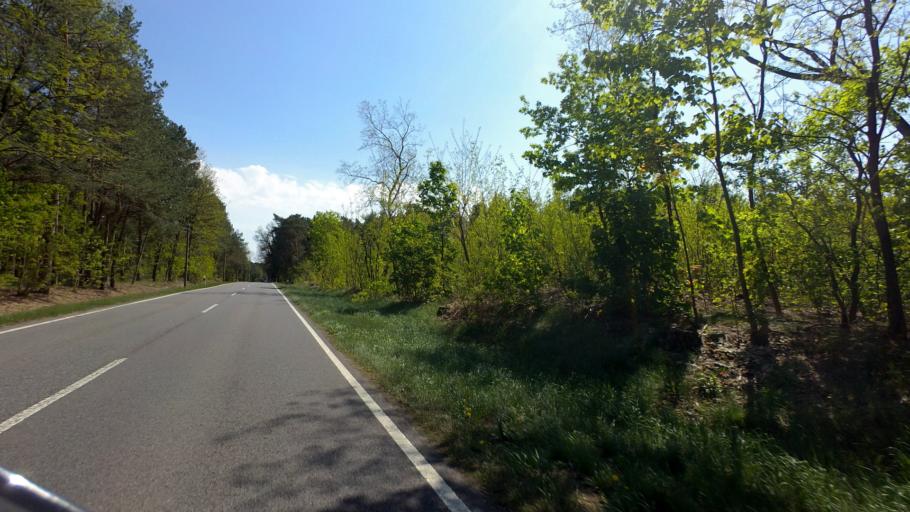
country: DE
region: Brandenburg
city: Lieberose
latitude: 52.0038
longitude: 14.1957
